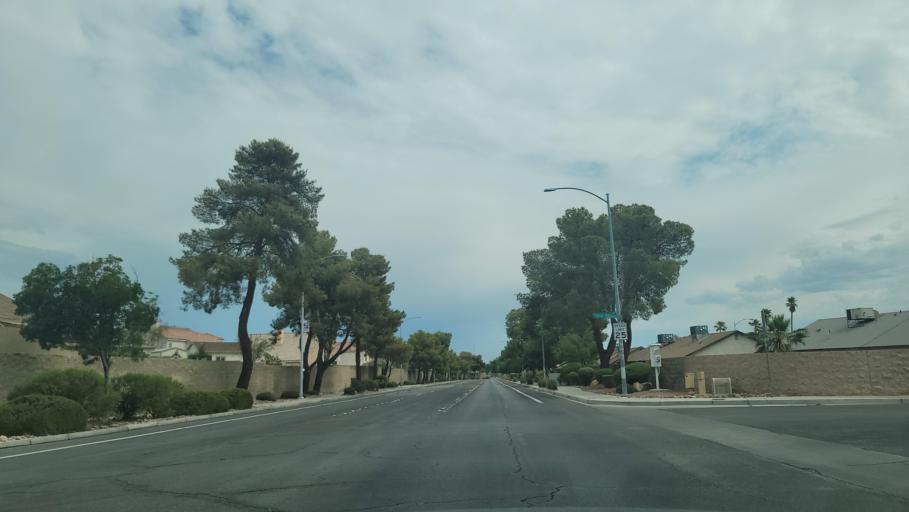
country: US
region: Nevada
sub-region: Clark County
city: Spring Valley
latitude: 36.1074
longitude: -115.2491
